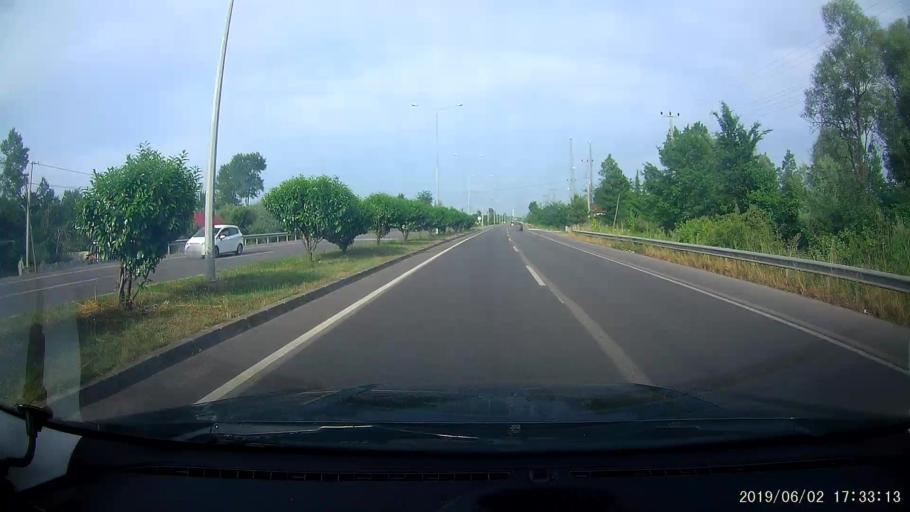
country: TR
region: Samsun
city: Carsamba
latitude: 41.2208
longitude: 36.8439
